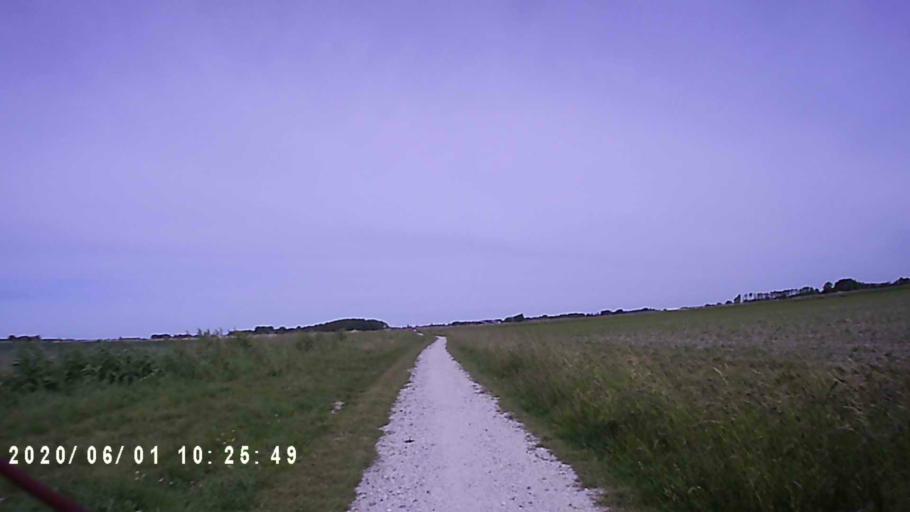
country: NL
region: Friesland
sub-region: Gemeente Het Bildt
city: Minnertsga
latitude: 53.2332
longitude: 5.6190
